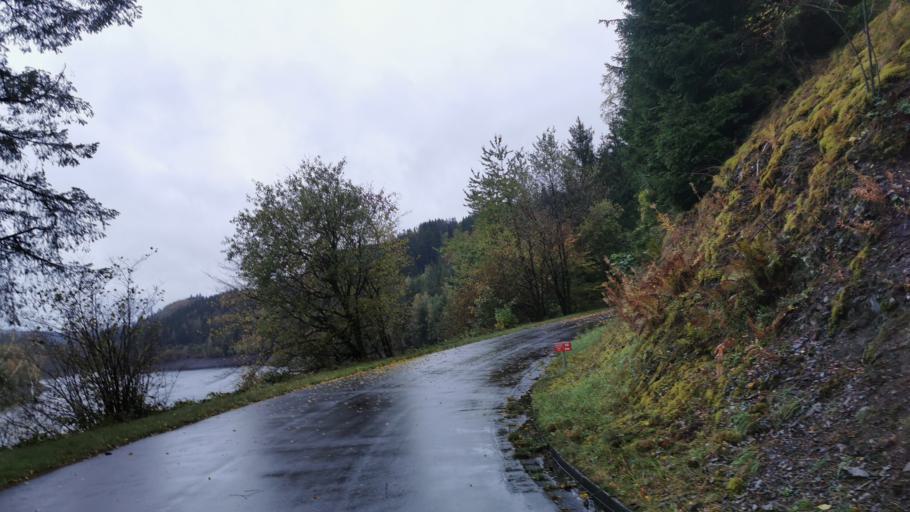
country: DE
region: Bavaria
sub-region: Upper Franconia
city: Steinwiesen
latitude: 50.3302
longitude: 11.4914
